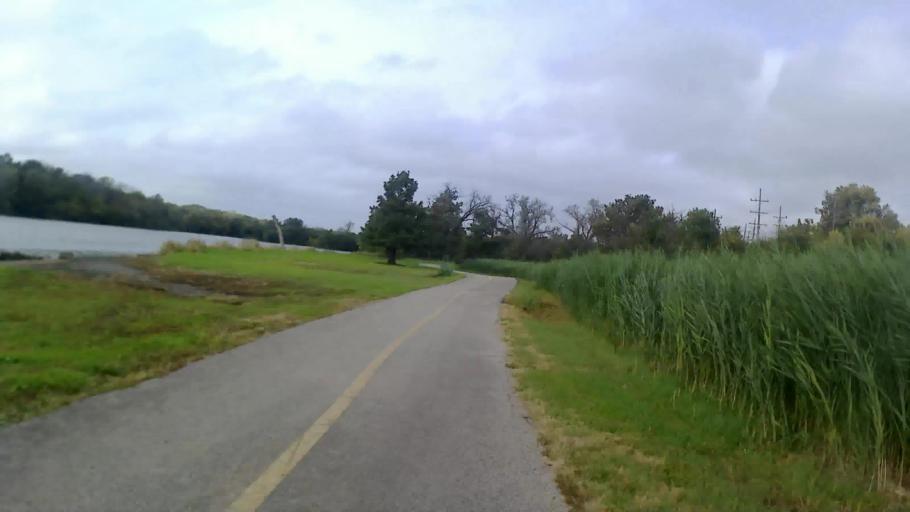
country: US
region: Illinois
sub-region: Kane County
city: Aurora
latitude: 41.7727
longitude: -88.3085
